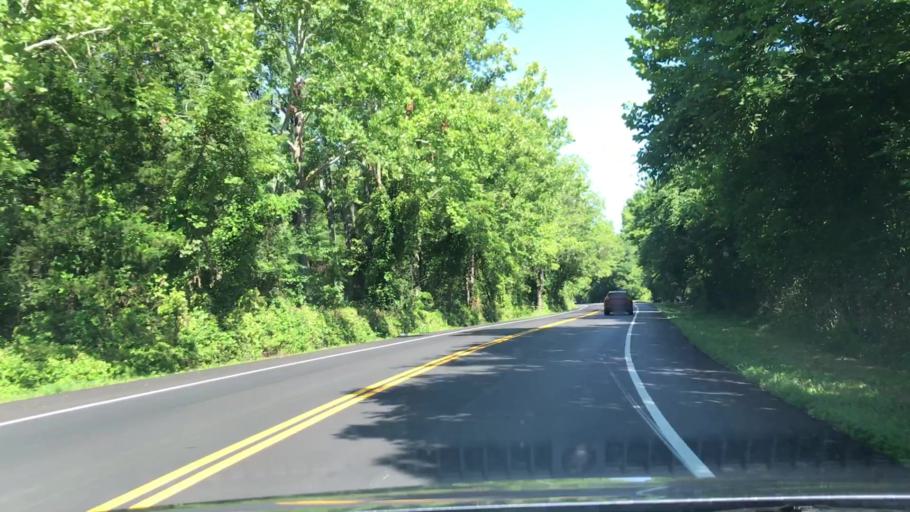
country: US
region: Tennessee
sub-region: Williamson County
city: Franklin
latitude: 35.9729
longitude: -86.8678
